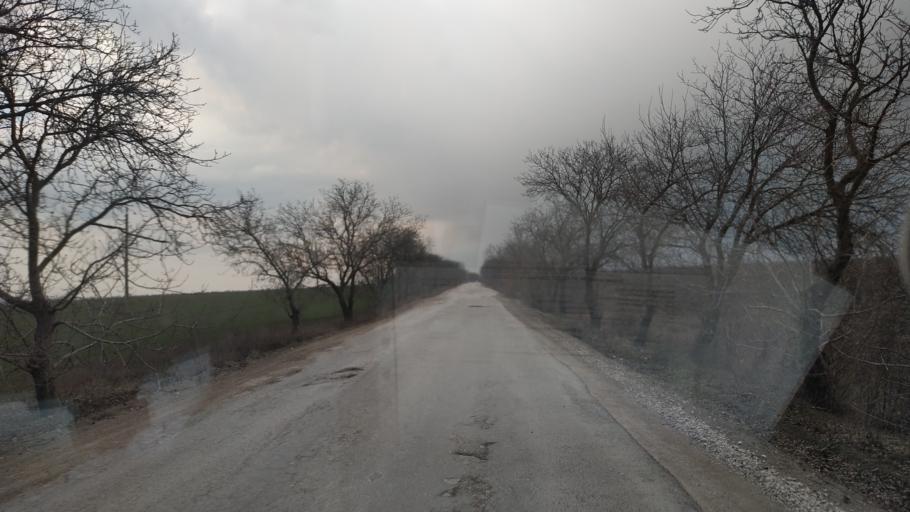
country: MD
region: Telenesti
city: Grigoriopol
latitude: 47.0378
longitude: 29.2935
